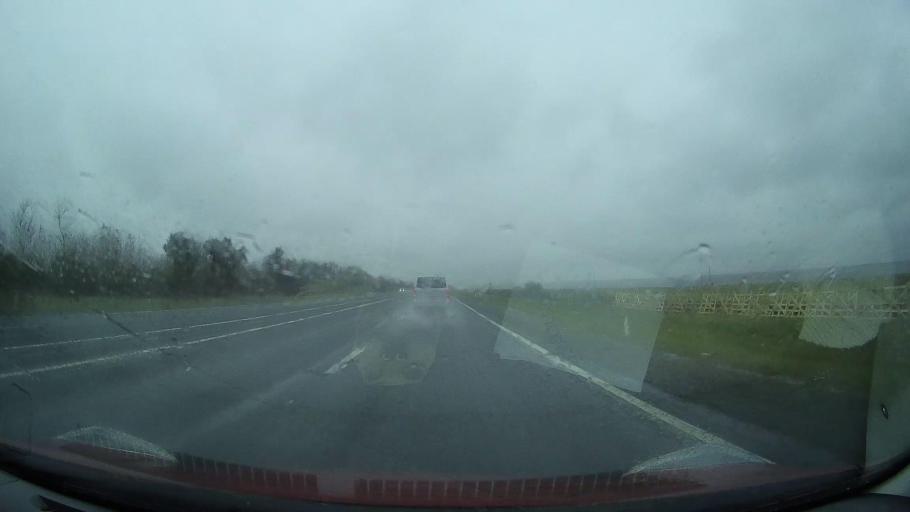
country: RU
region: Stavropol'skiy
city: Nevinnomyssk
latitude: 44.6124
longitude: 42.1180
